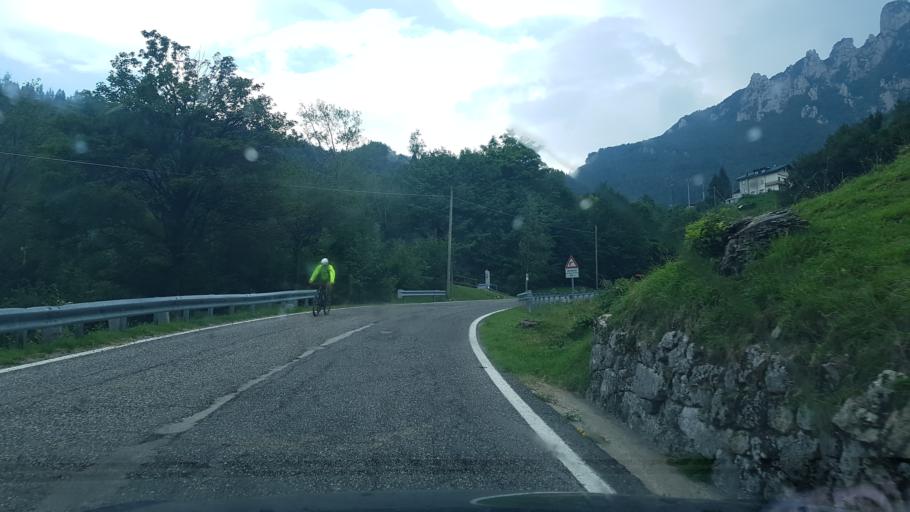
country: IT
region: Veneto
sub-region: Provincia di Vicenza
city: Recoaro Terme
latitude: 45.7614
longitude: 11.1950
